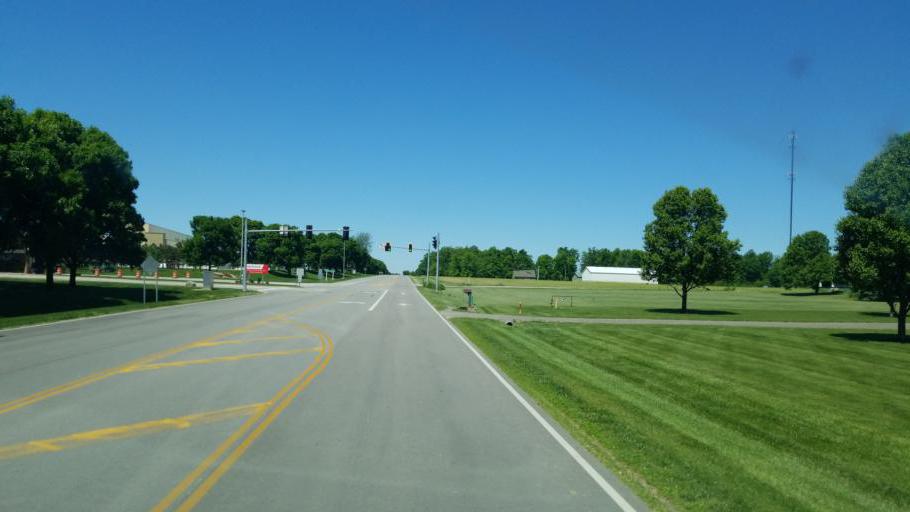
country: US
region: Ohio
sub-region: Shelby County
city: Anna
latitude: 40.3805
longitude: -84.1858
